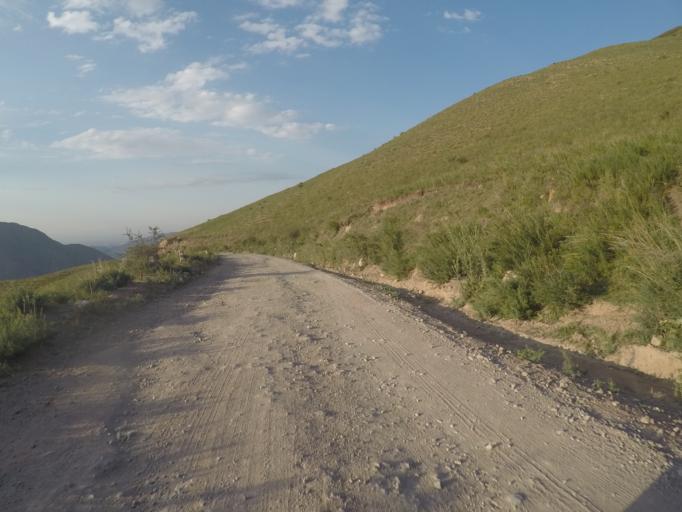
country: KG
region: Chuy
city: Bishkek
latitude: 42.6543
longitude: 74.6628
